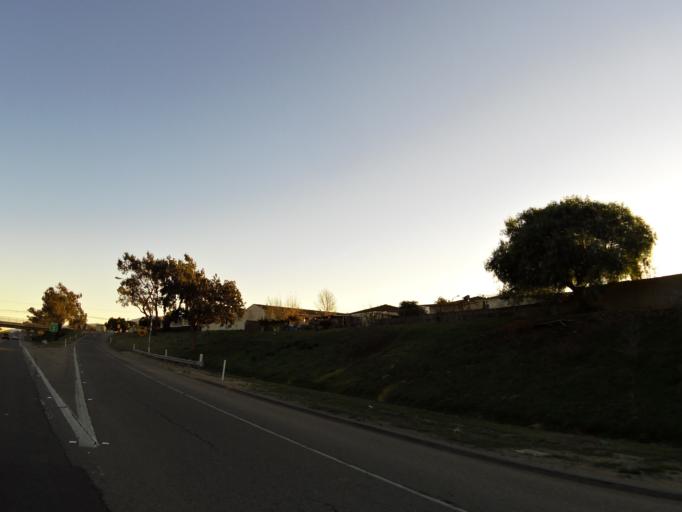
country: US
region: California
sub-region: Monterey County
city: Gonzales
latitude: 36.5153
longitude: -121.4389
